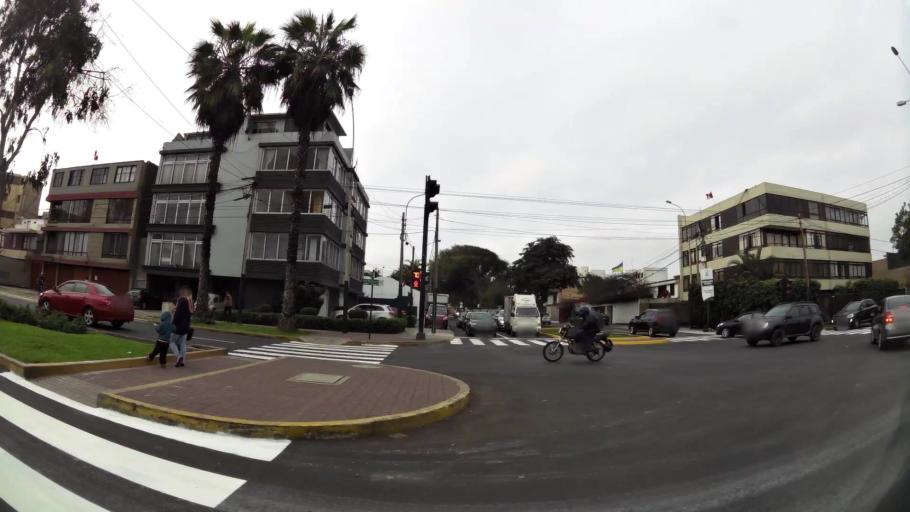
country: PE
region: Lima
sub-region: Lima
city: San Isidro
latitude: -12.1078
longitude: -77.0540
